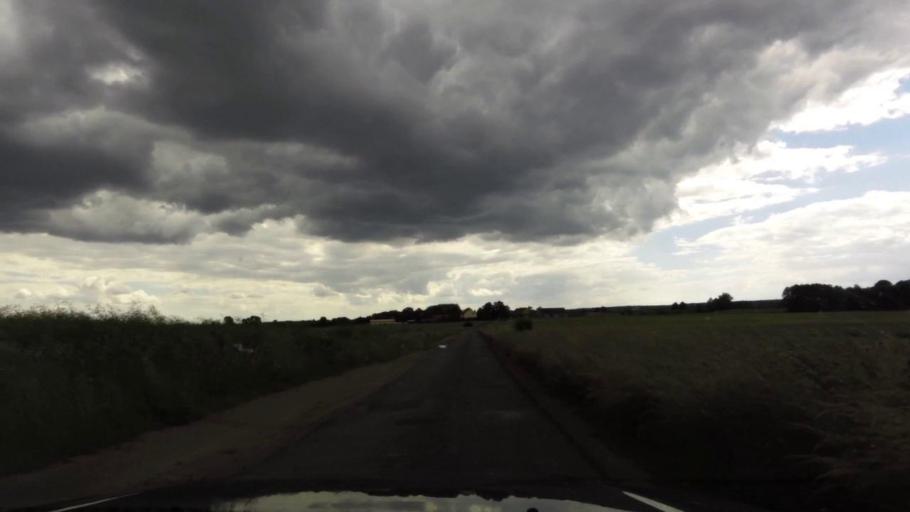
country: PL
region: West Pomeranian Voivodeship
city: Trzcinsko Zdroj
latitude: 52.9442
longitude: 14.6024
